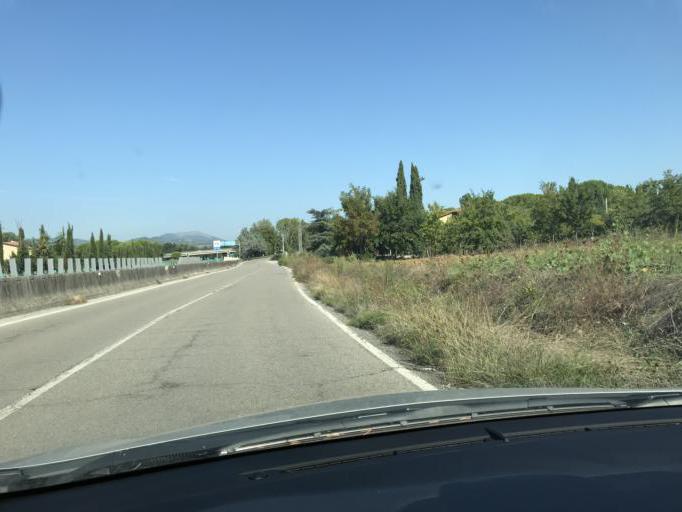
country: IT
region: Umbria
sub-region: Provincia di Perugia
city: Via Lippia
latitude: 43.1053
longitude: 12.4766
